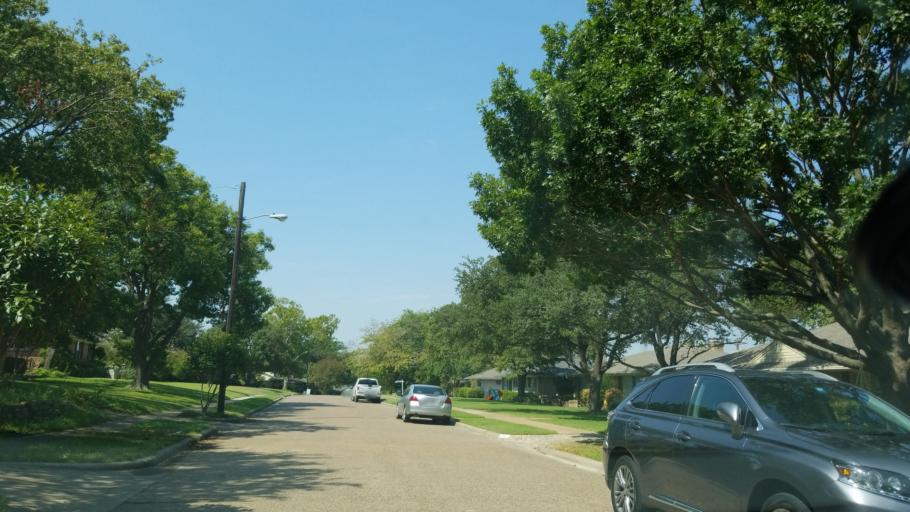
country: US
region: Texas
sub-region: Dallas County
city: Richardson
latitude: 32.8758
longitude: -96.7151
